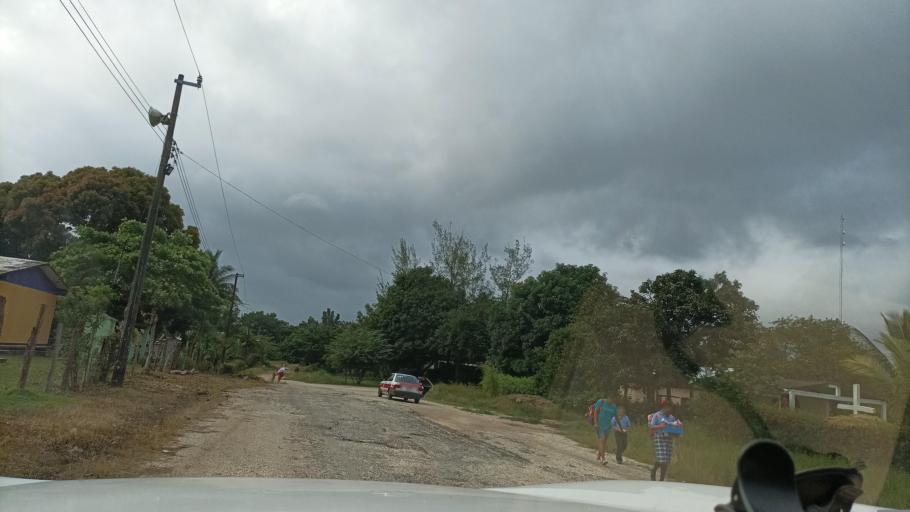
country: MX
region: Veracruz
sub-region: Moloacan
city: Cuichapa
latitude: 17.9221
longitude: -94.3683
